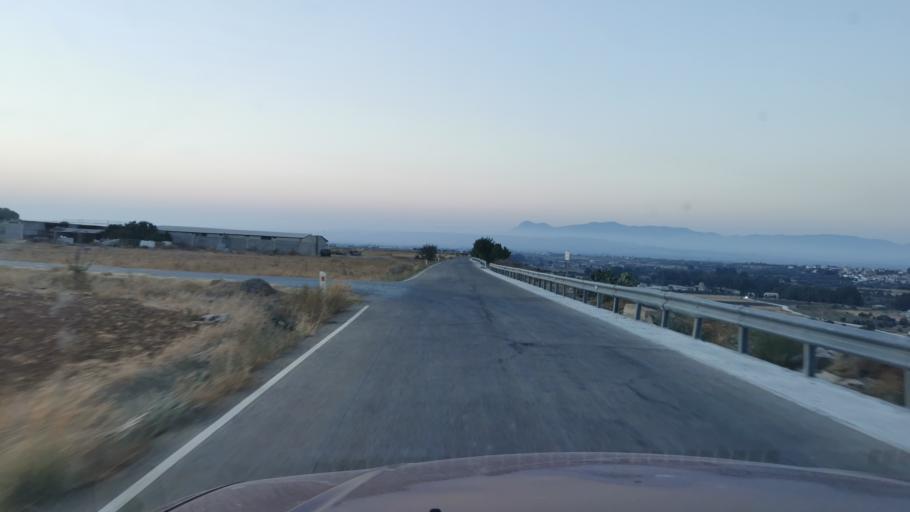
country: CY
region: Lefkosia
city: Peristerona
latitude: 35.0901
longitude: 33.0822
